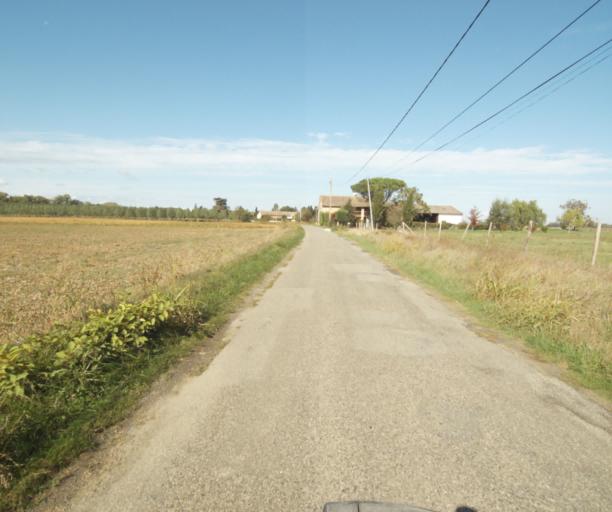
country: FR
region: Midi-Pyrenees
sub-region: Departement du Tarn-et-Garonne
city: Verdun-sur-Garonne
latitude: 43.8677
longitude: 1.2428
